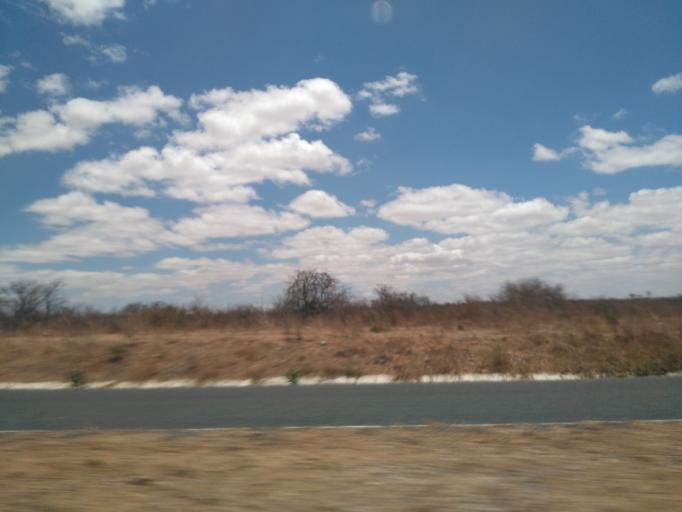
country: TZ
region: Dodoma
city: Kisasa
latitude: -6.1690
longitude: 35.8460
